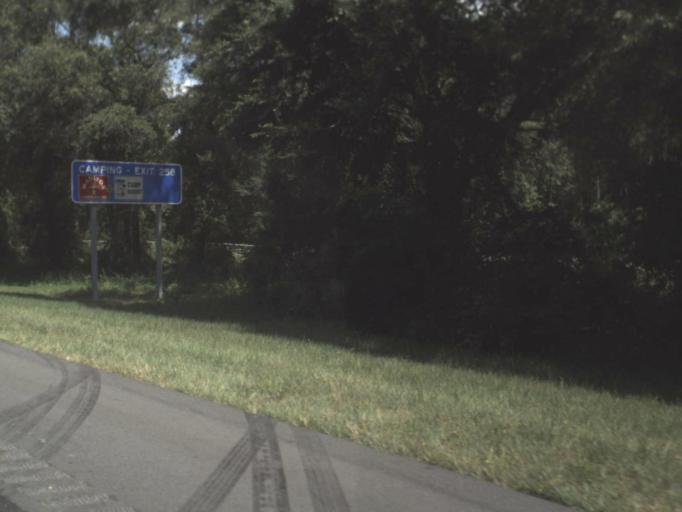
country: US
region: Florida
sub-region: Madison County
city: Madison
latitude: 30.3922
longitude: -83.3395
